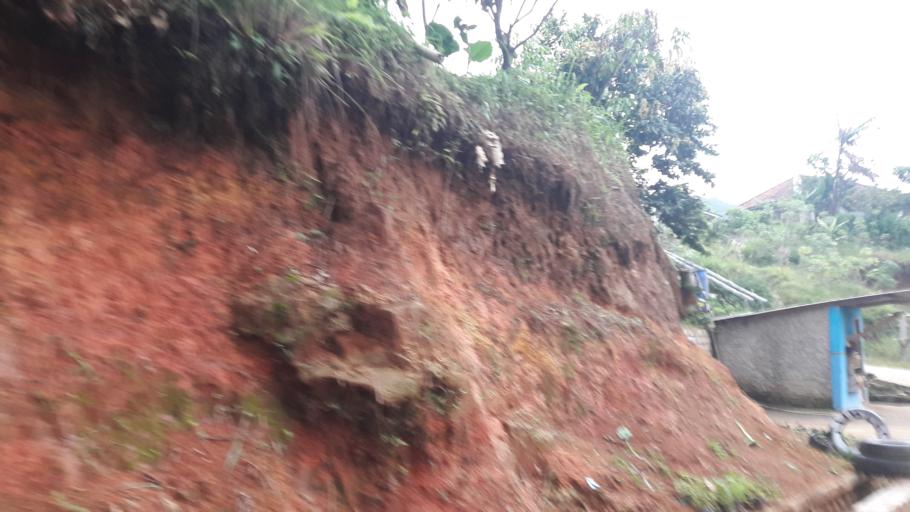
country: ID
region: West Java
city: Cipeundeuy
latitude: -6.6785
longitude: 106.5194
